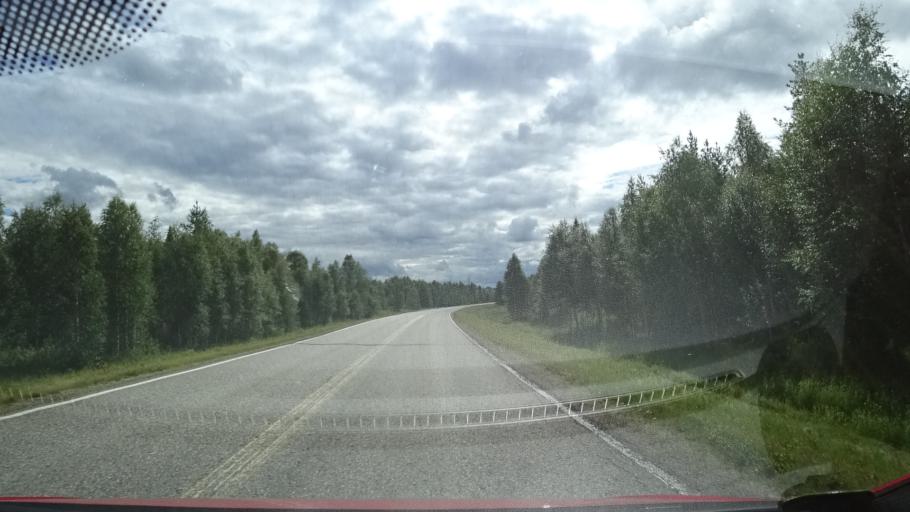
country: FI
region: Lapland
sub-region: Tunturi-Lappi
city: Kittilae
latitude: 67.4668
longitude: 24.9485
